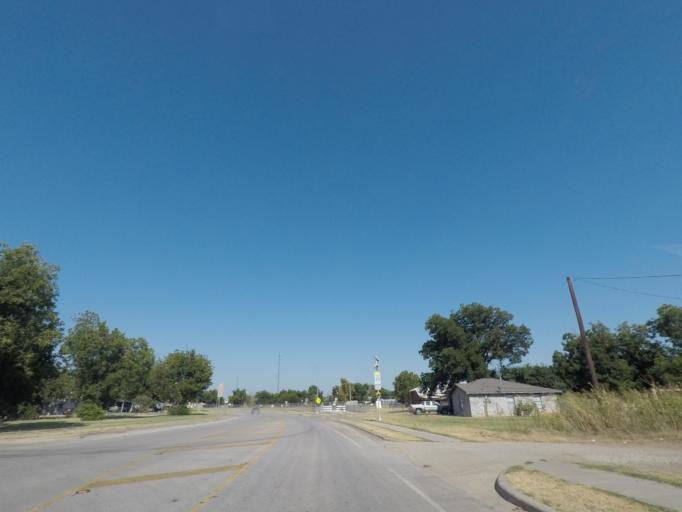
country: US
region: Texas
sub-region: Baylor County
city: Seymour
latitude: 33.5943
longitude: -99.2599
